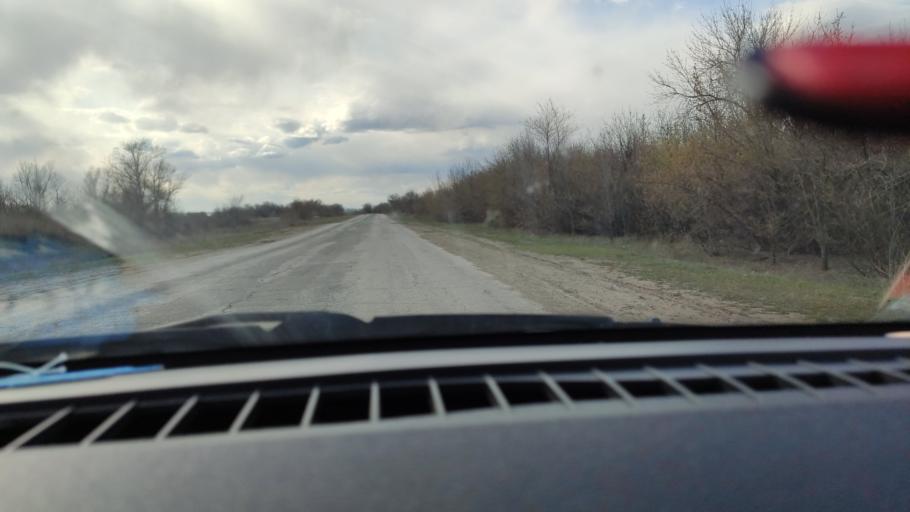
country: RU
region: Saratov
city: Rovnoye
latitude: 51.0445
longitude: 46.0589
